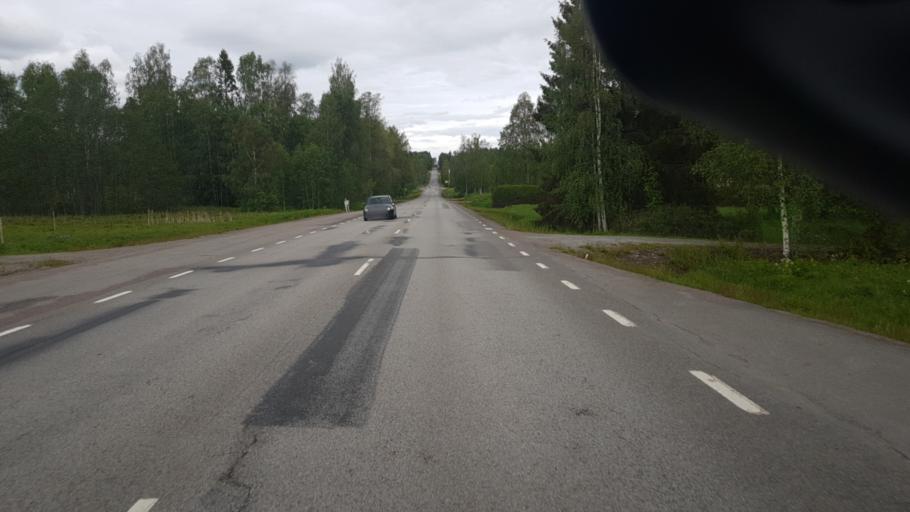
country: SE
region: Vaermland
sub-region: Arvika Kommun
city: Arvika
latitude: 59.6796
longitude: 12.6306
